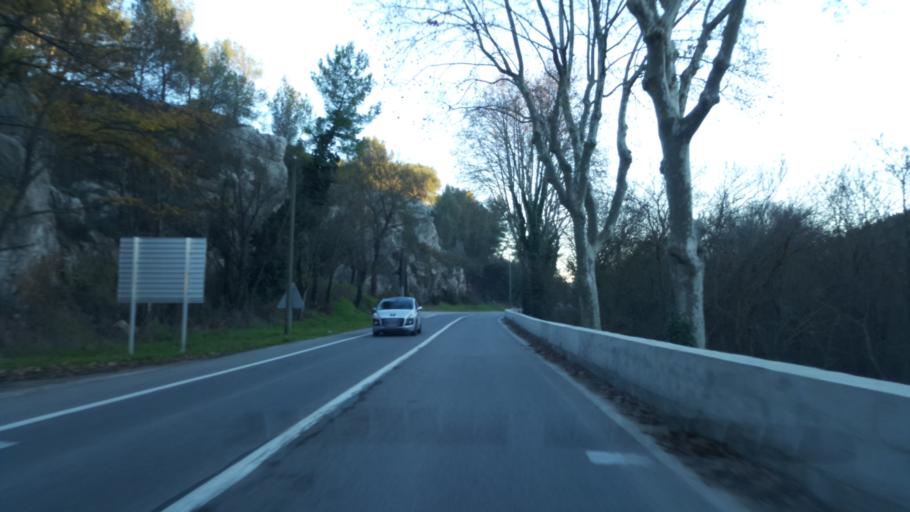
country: FR
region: Provence-Alpes-Cote d'Azur
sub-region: Departement des Bouches-du-Rhone
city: Le Tholonet
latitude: 43.5008
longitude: 5.5165
